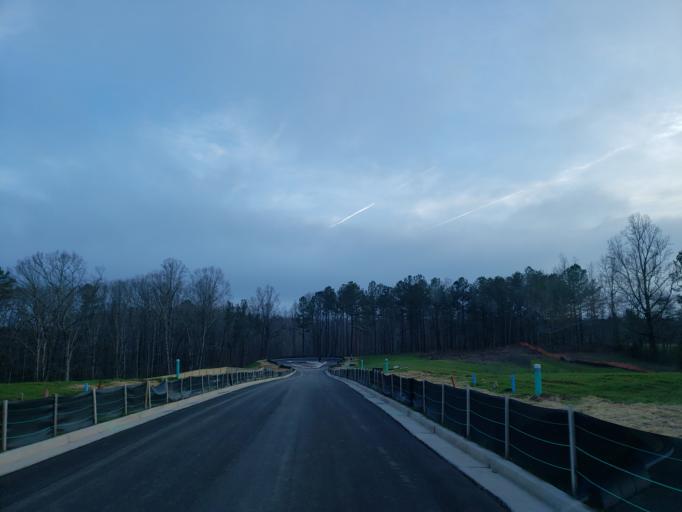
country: US
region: Georgia
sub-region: Cherokee County
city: Ball Ground
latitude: 34.2377
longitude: -84.3392
